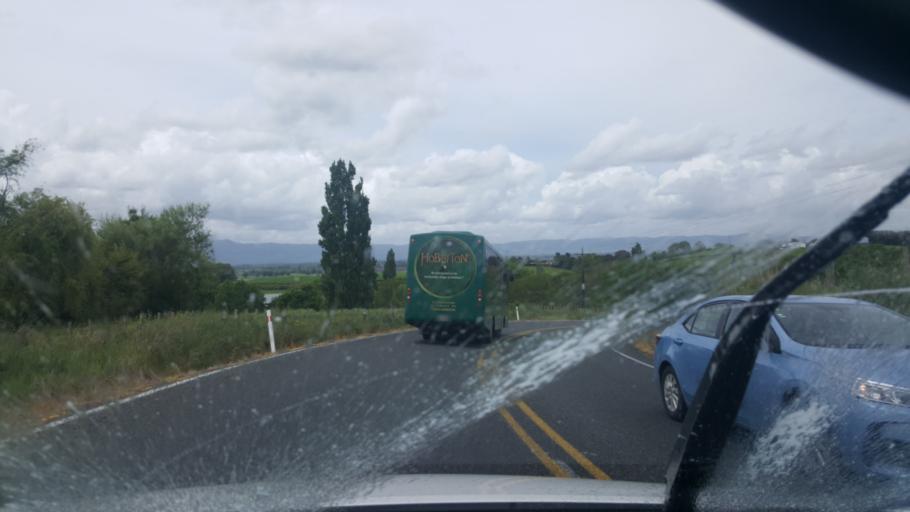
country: NZ
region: Waikato
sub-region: Matamata-Piako District
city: Matamata
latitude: -37.8791
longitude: 175.6917
